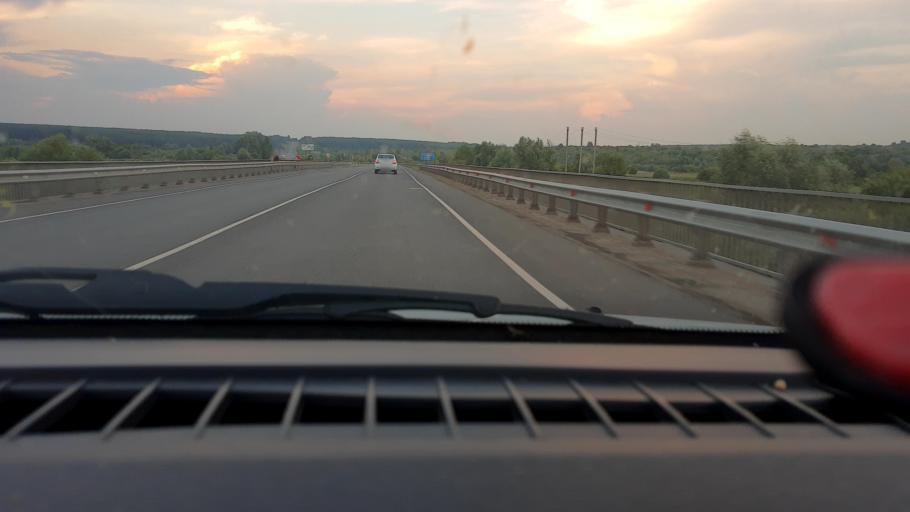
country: RU
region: Nizjnij Novgorod
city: Arzamas
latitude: 55.3321
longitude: 43.8889
